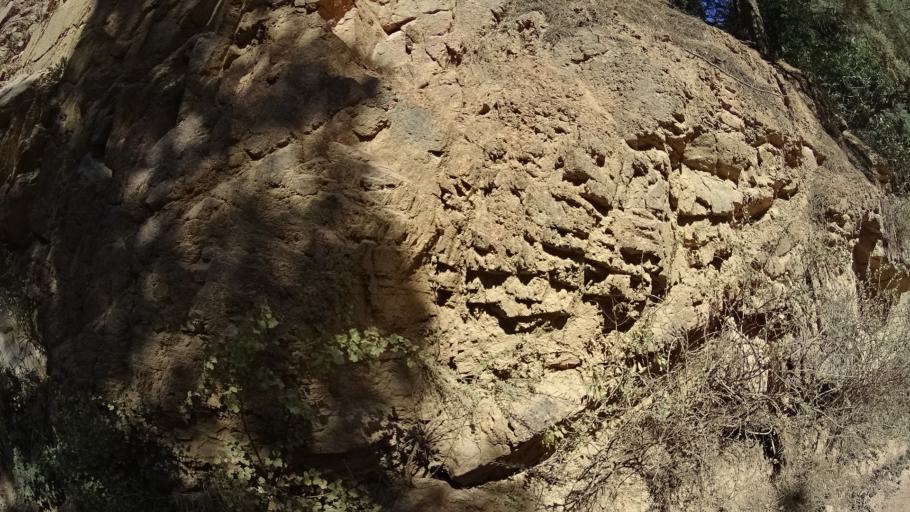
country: US
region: Colorado
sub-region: El Paso County
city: Manitou Springs
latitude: 38.7947
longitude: -104.8977
